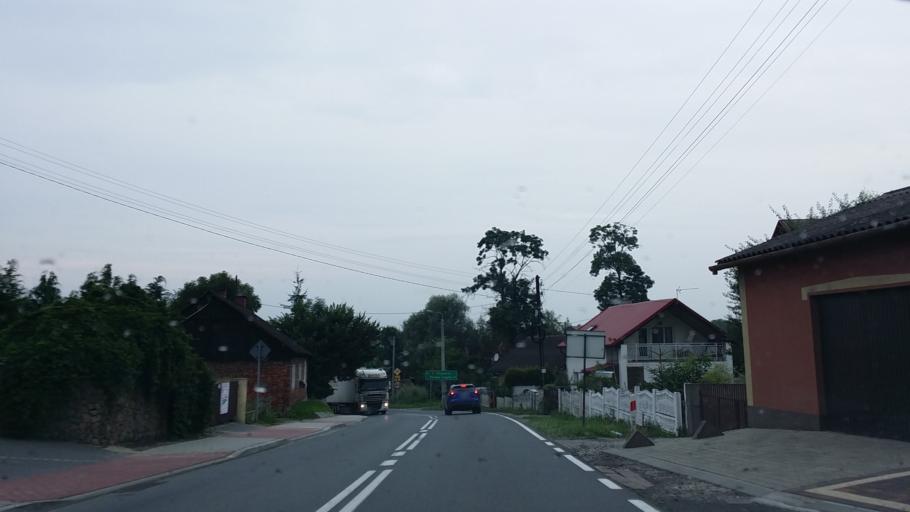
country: PL
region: Lesser Poland Voivodeship
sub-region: Powiat wadowicki
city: Spytkowice
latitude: 49.9959
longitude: 19.5134
